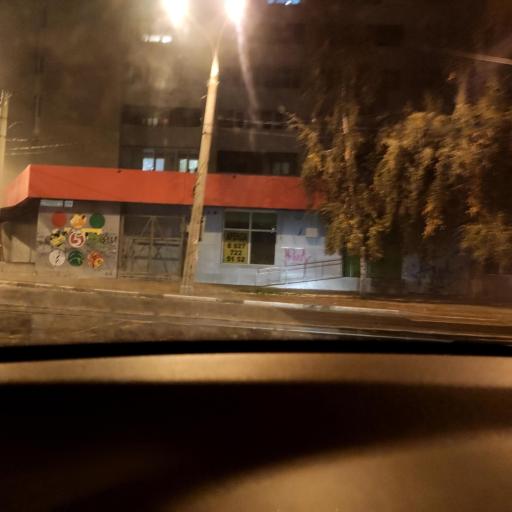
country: RU
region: Samara
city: Samara
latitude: 53.2060
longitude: 50.1219
